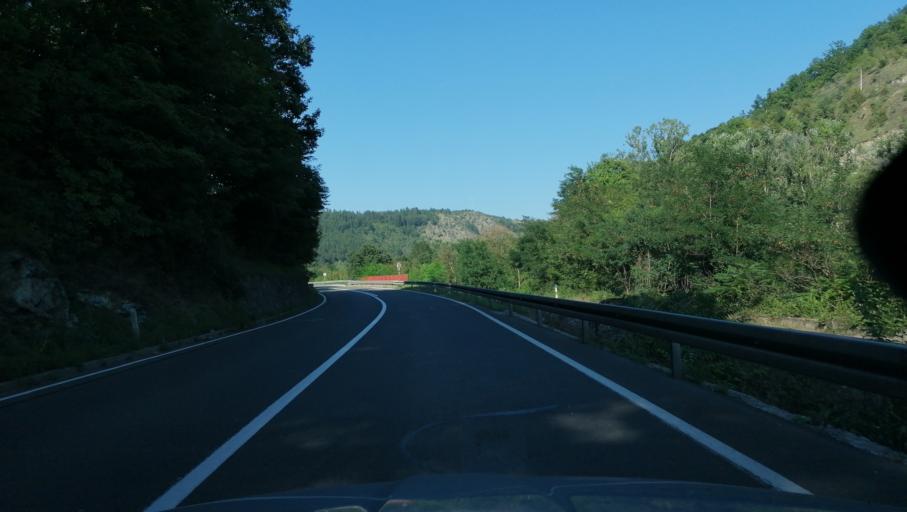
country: RS
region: Central Serbia
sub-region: Raski Okrug
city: Kraljevo
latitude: 43.6602
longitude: 20.5633
